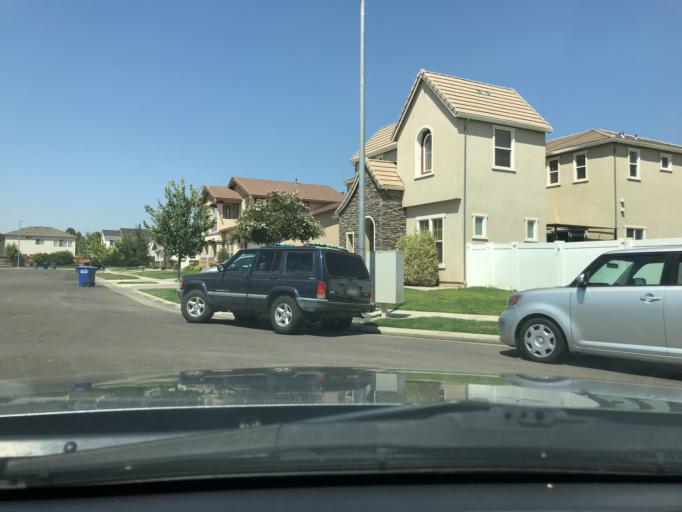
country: US
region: California
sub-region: Merced County
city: Merced
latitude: 37.3605
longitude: -120.4704
